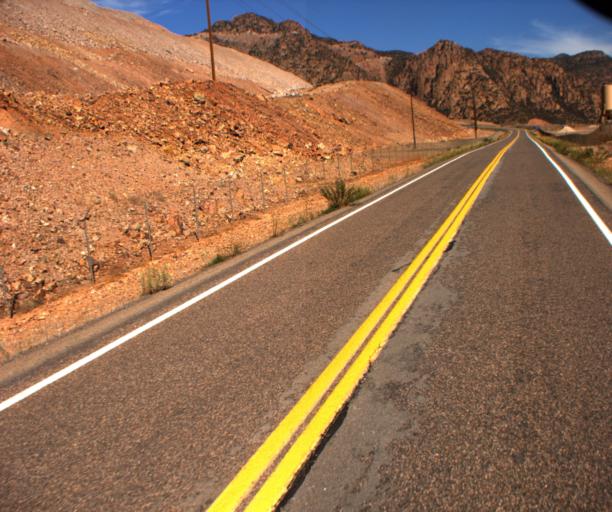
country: US
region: Arizona
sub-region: Greenlee County
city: Morenci
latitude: 33.1242
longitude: -109.3674
